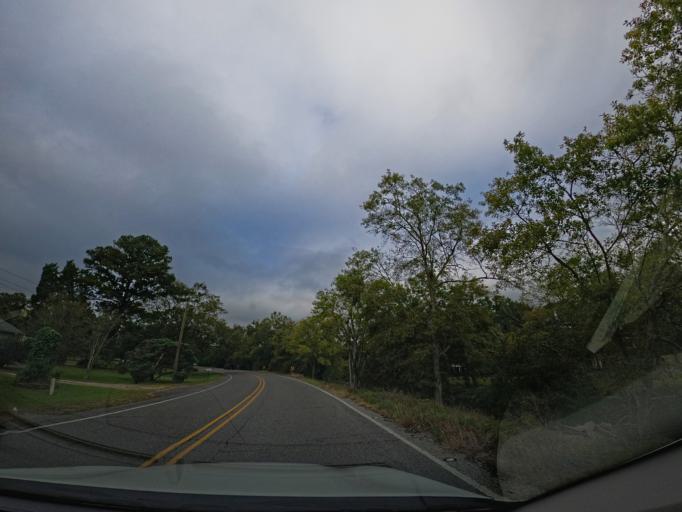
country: US
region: Louisiana
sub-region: Terrebonne Parish
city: Houma
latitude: 29.5743
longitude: -90.7551
